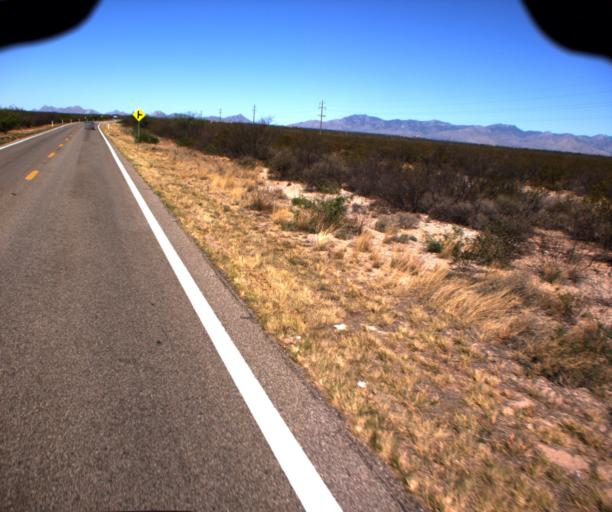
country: US
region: Arizona
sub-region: Cochise County
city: Tombstone
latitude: 31.7216
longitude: -110.2108
